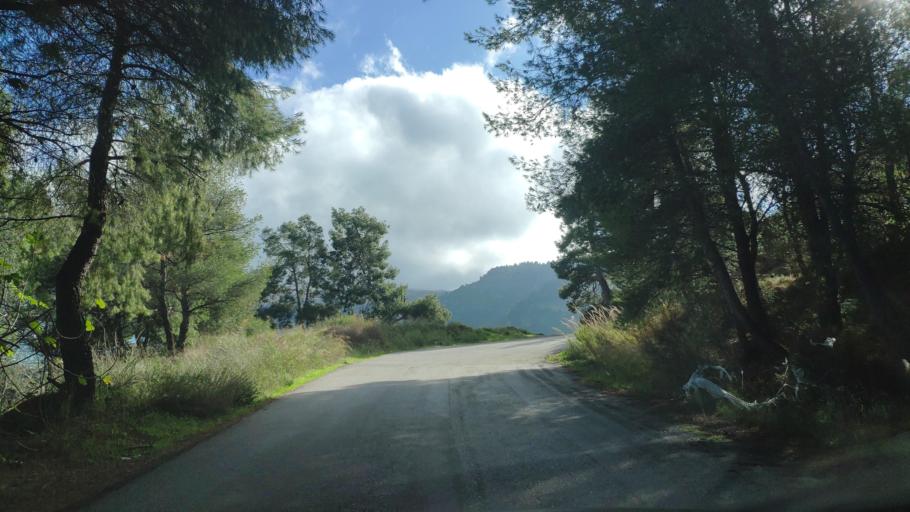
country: GR
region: West Greece
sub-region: Nomos Achaias
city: Aiyira
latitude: 38.0996
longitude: 22.4461
